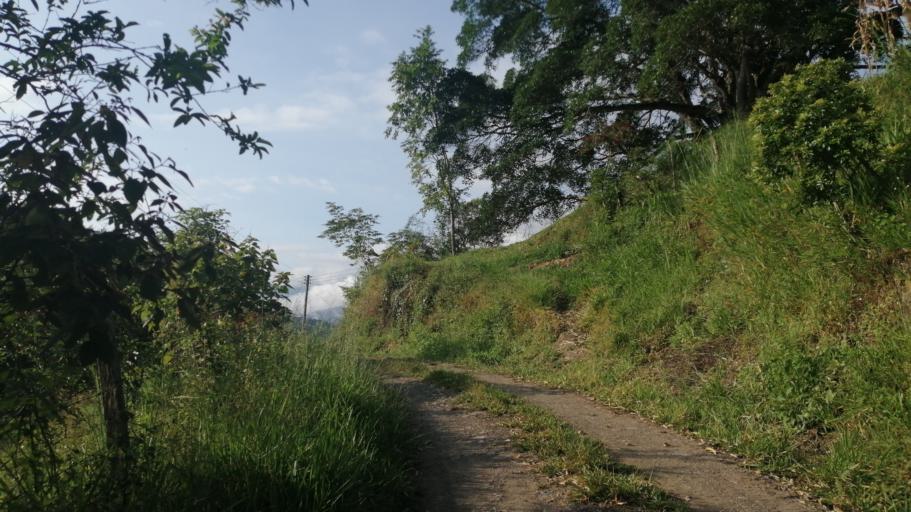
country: CO
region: Boyaca
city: Garagoa
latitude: 5.0739
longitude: -73.3890
